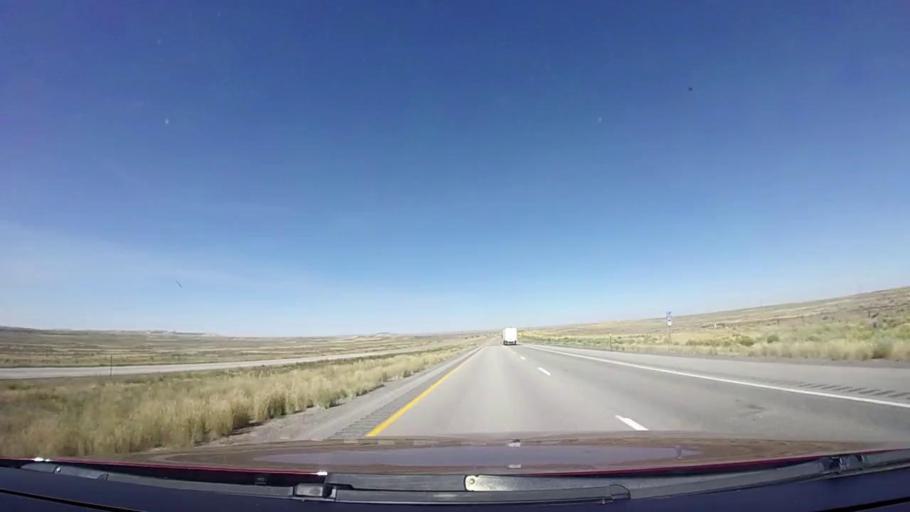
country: US
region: Wyoming
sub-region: Sweetwater County
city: Rock Springs
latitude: 41.6322
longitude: -108.3566
